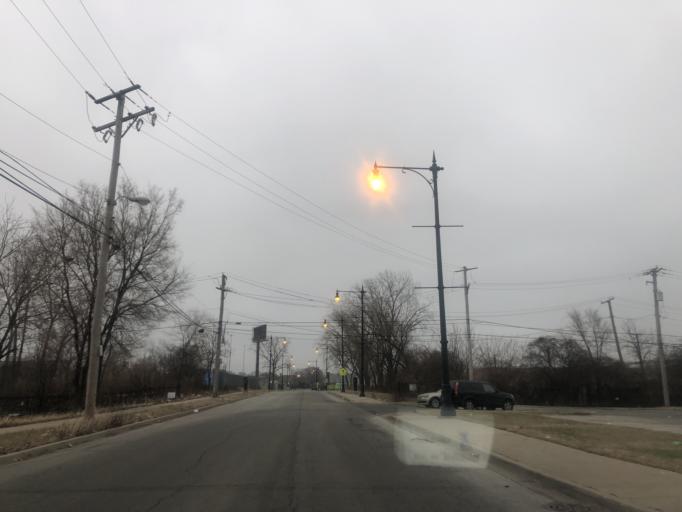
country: US
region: Illinois
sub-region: Cook County
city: Evergreen Park
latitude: 41.7399
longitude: -87.6299
